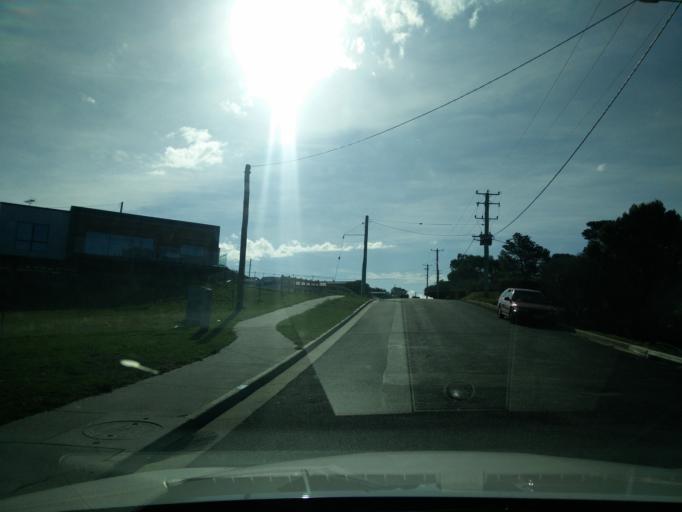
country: AU
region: Tasmania
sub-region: Break O'Day
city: St Helens
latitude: -41.4632
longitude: 148.2631
